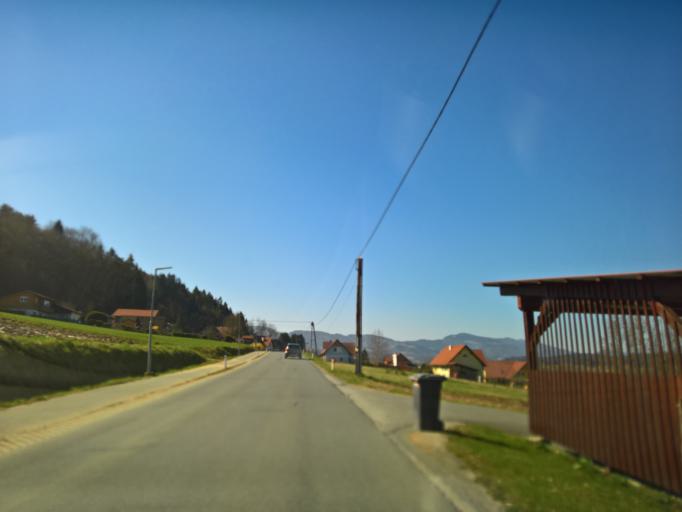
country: AT
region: Styria
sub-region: Politischer Bezirk Leibnitz
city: Sankt Johann im Saggautal
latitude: 46.7127
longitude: 15.4079
